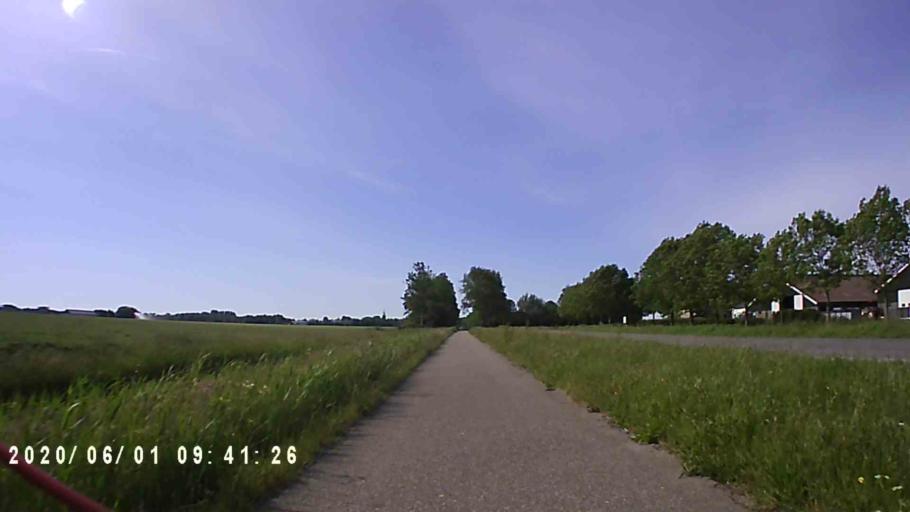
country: NL
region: Friesland
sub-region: Menameradiel
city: Berltsum
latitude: 53.2483
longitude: 5.6821
